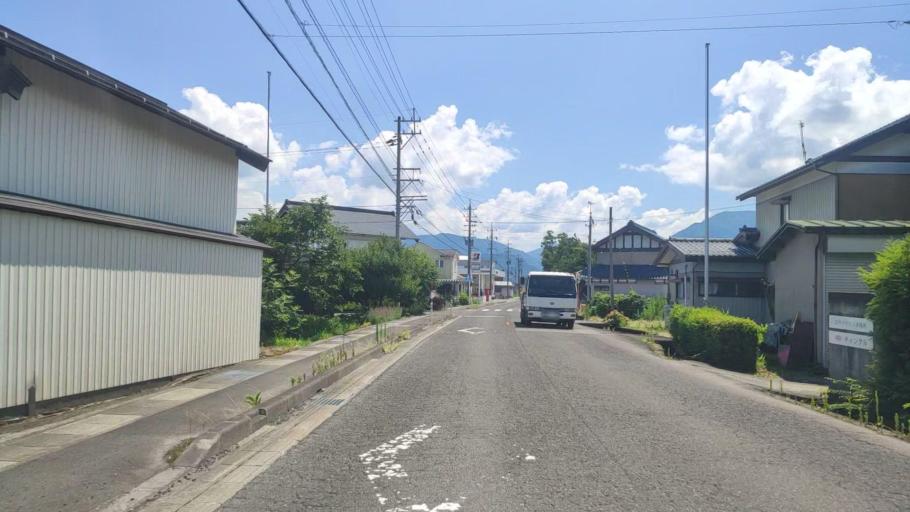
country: JP
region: Fukui
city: Ono
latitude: 35.9797
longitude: 136.5133
